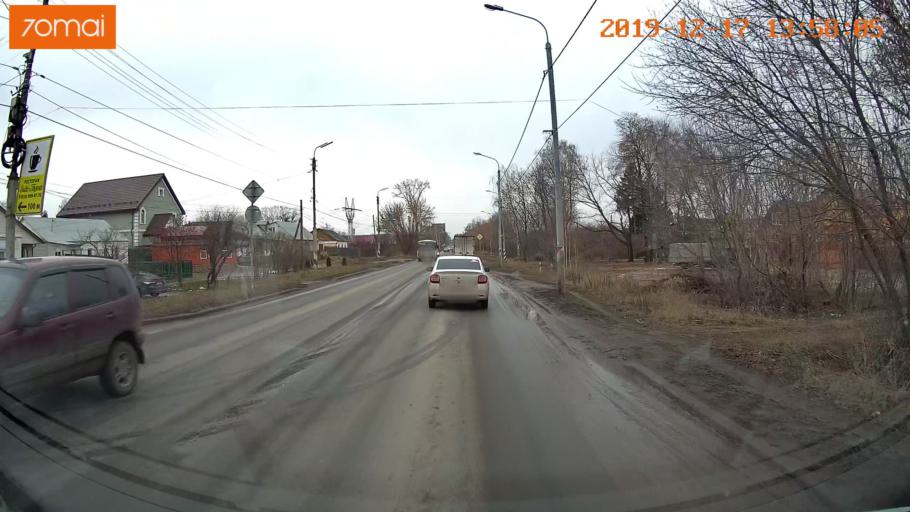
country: RU
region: Rjazan
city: Ryazan'
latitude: 54.6243
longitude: 39.6870
